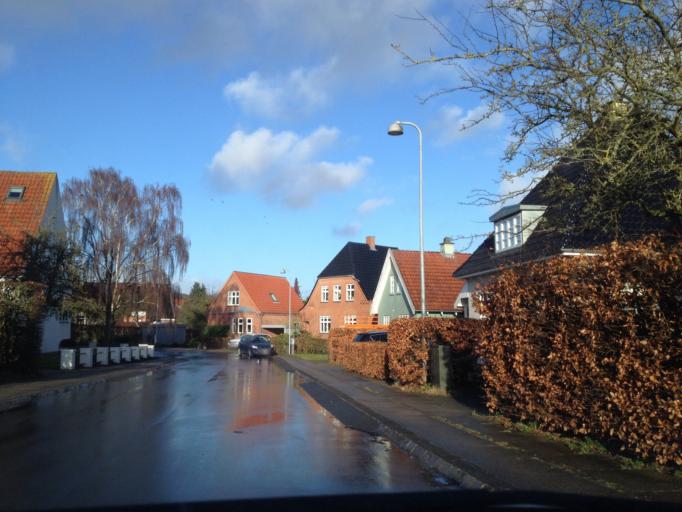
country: DK
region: South Denmark
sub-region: Odense Kommune
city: Odense
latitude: 55.3714
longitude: 10.3677
